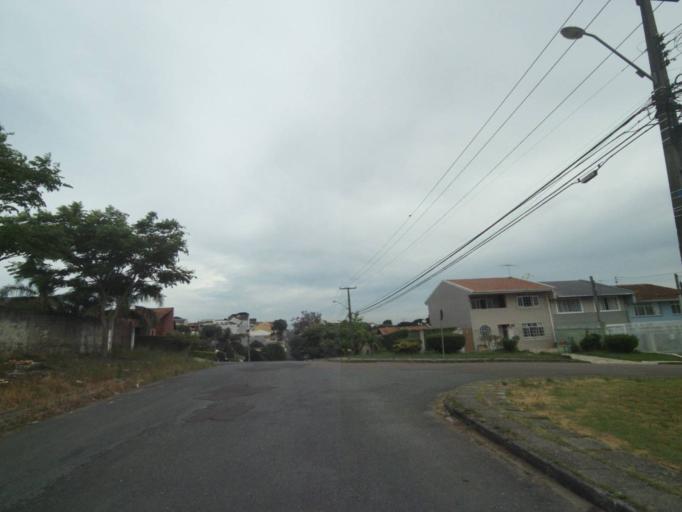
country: BR
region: Parana
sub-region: Pinhais
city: Pinhais
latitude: -25.4162
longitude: -49.2084
